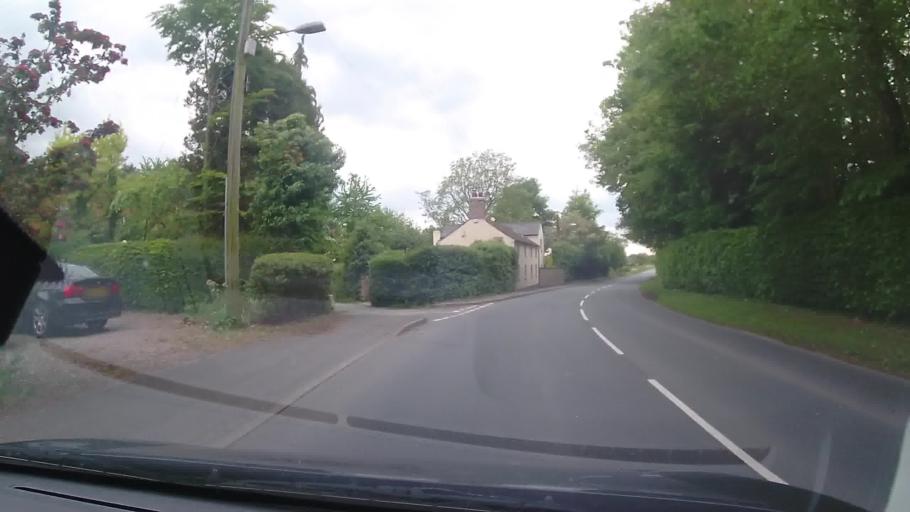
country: GB
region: Wales
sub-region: Wrexham
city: Overton
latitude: 52.9663
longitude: -2.9345
